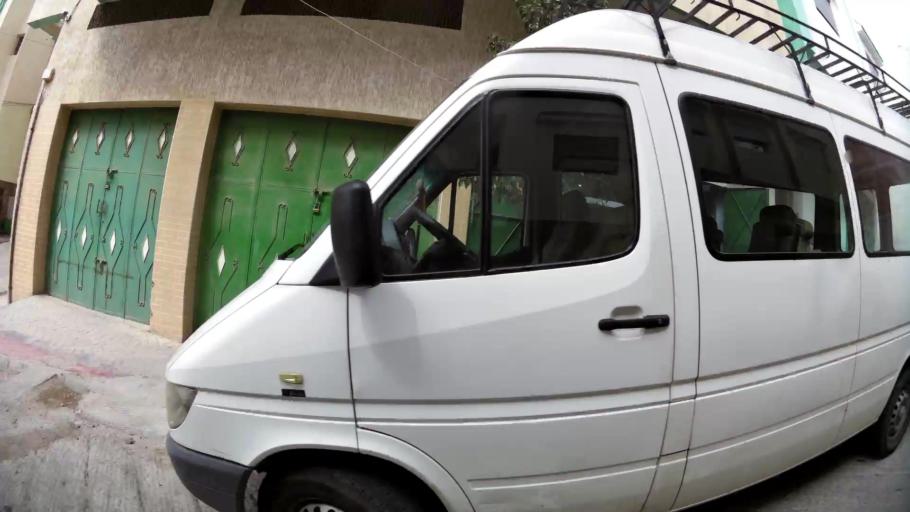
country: MA
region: Tanger-Tetouan
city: Tetouan
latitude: 35.5774
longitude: -5.3909
